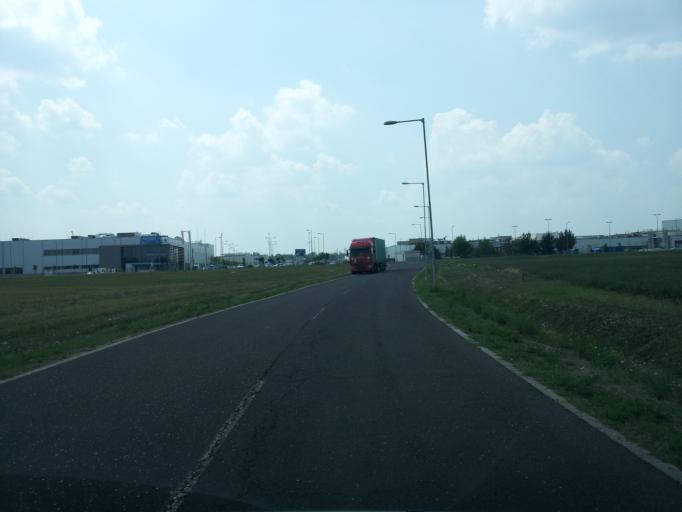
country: HU
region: Pest
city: Taksony
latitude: 47.3086
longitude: 19.0475
